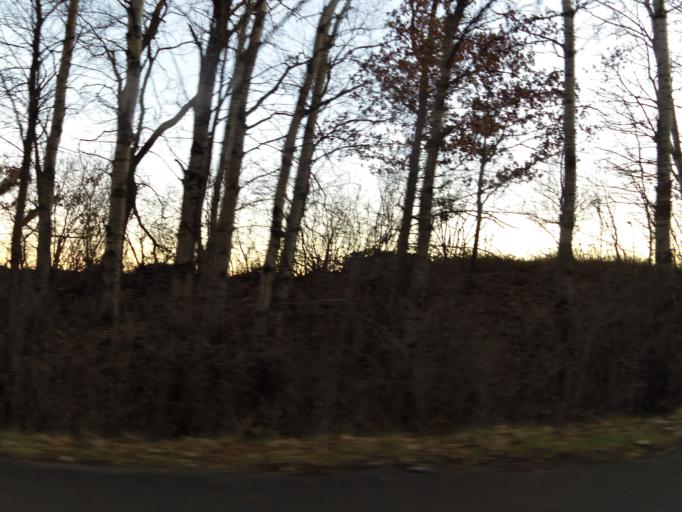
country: US
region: Minnesota
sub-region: Washington County
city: Grant
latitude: 45.0923
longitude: -92.8821
